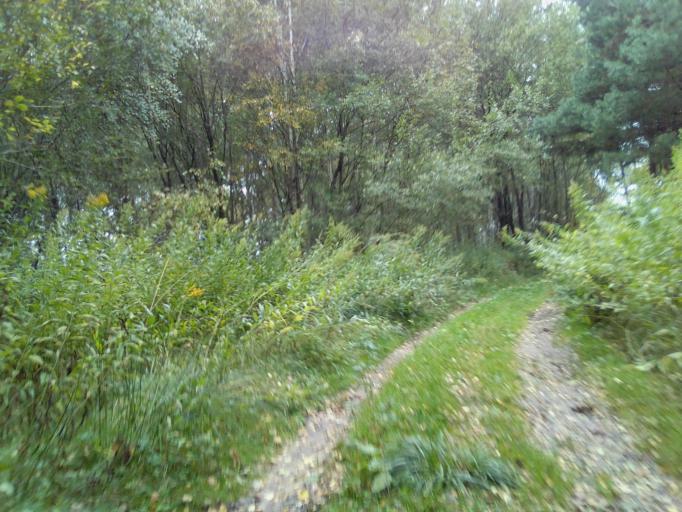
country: PL
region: Subcarpathian Voivodeship
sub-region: Powiat strzyzowski
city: Strzyzow
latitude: 49.8525
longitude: 21.8419
